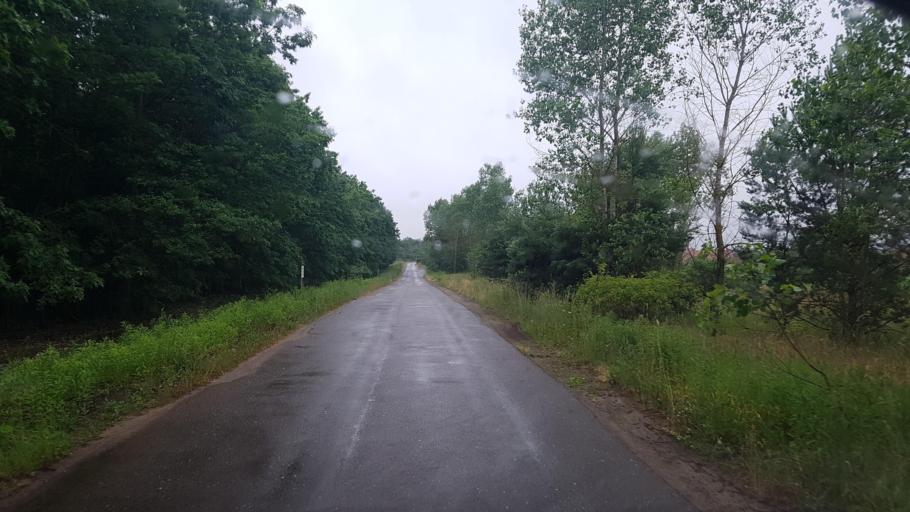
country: DE
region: Brandenburg
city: Lauchhammer
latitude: 51.5411
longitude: 13.7520
